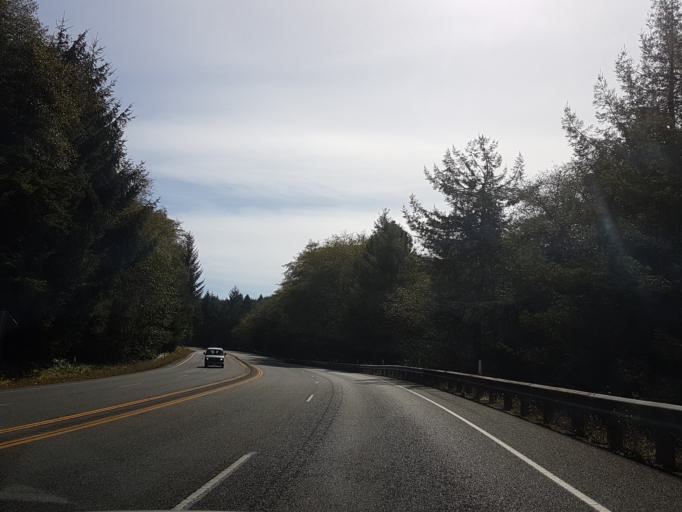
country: US
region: California
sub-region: Del Norte County
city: Bertsch-Oceanview
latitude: 41.4865
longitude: -124.0509
